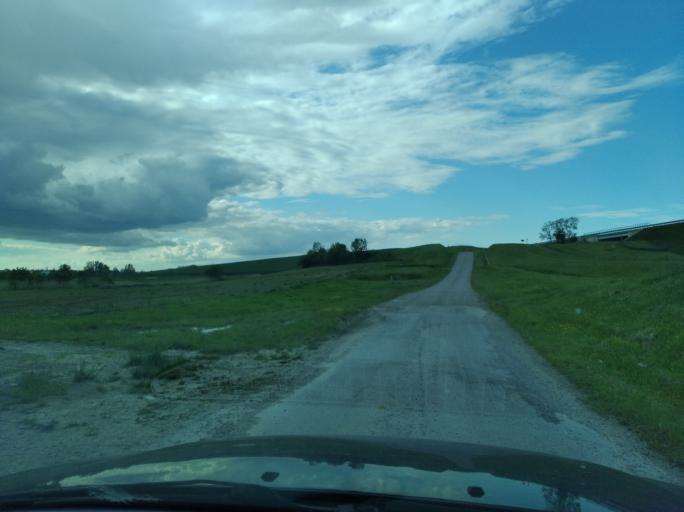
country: PL
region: Subcarpathian Voivodeship
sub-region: Powiat jaroslawski
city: Pawlosiow
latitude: 49.9508
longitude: 22.6614
